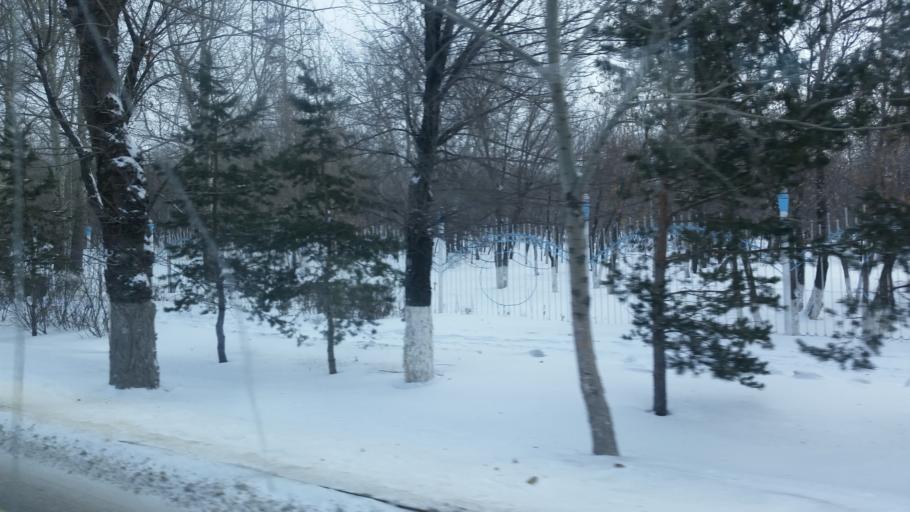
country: KZ
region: Qaraghandy
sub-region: Qaraghandy Qalasy
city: Karagandy
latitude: 49.8132
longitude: 73.0751
